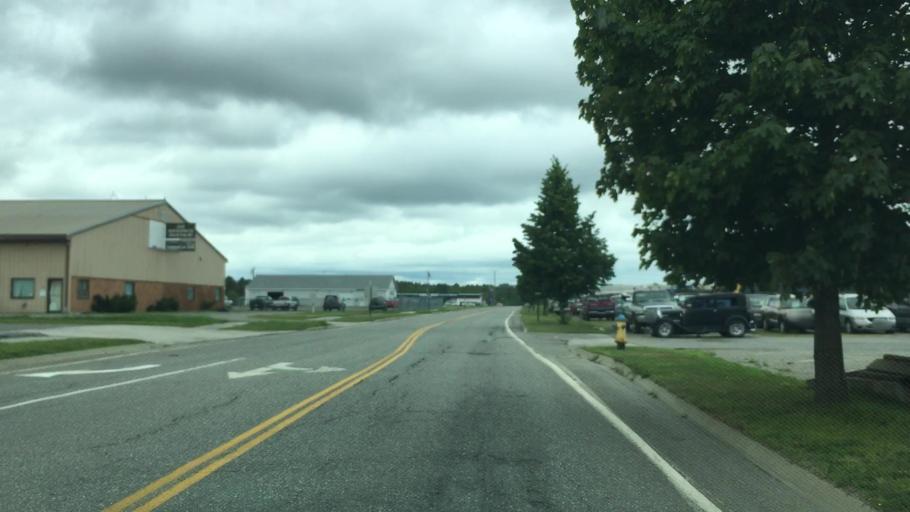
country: US
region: Maine
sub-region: Penobscot County
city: Brewer
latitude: 44.7755
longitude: -68.7390
